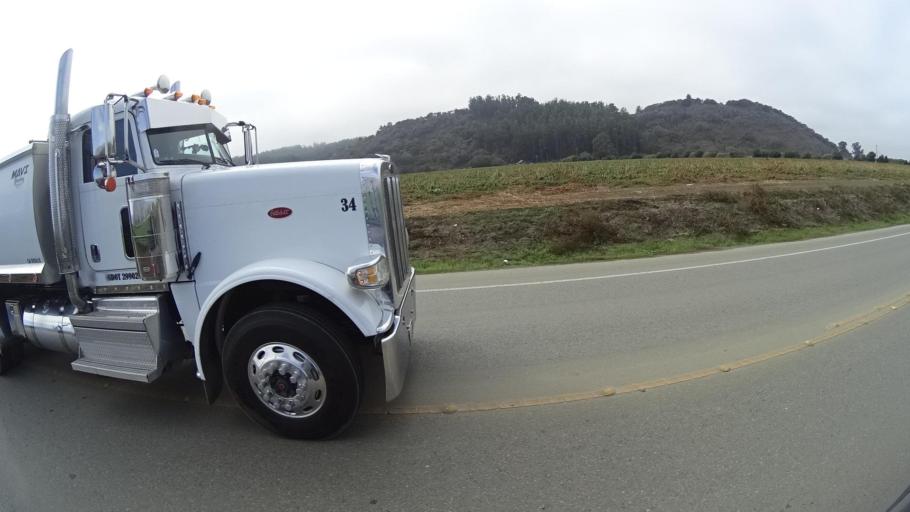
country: US
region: California
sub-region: Monterey County
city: Pajaro
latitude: 36.9039
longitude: -121.7008
